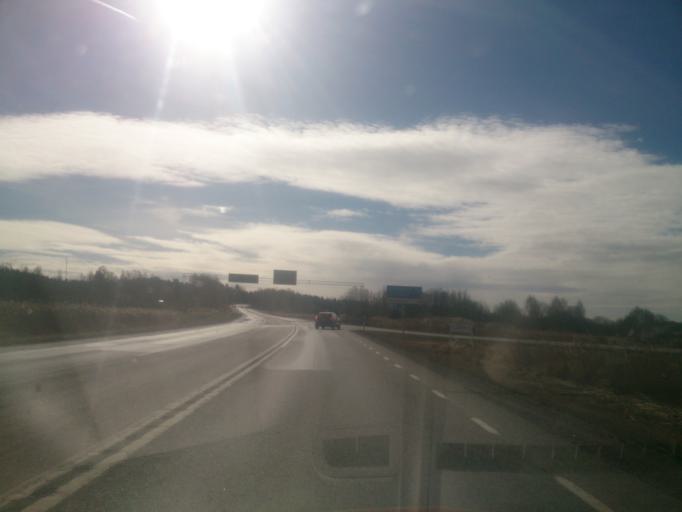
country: SE
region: OEstergoetland
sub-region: Norrkopings Kommun
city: Kimstad
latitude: 58.5124
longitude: 15.9815
